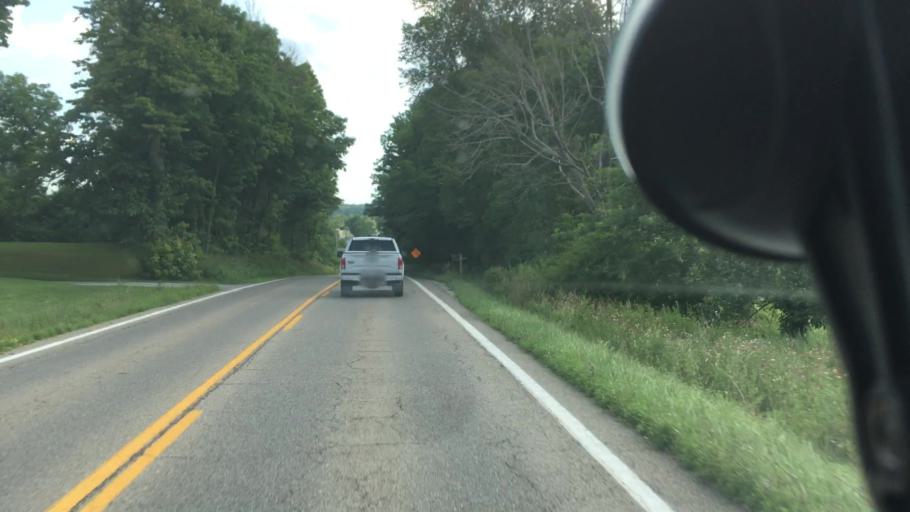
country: US
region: Ohio
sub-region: Columbiana County
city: Salem
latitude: 40.9633
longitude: -80.8303
